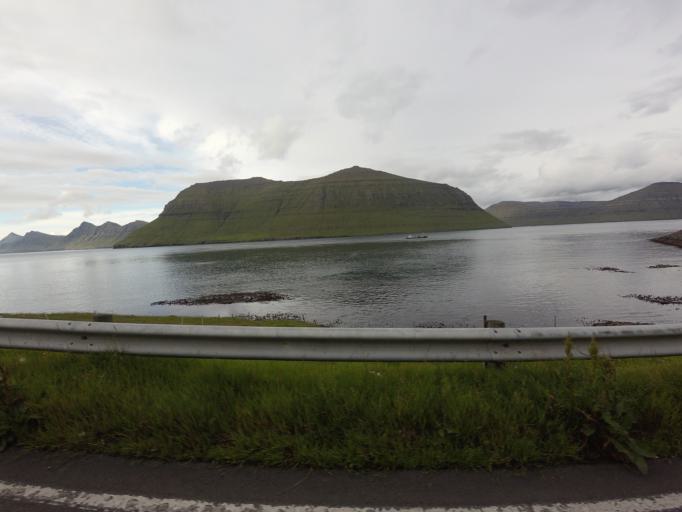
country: FO
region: Eysturoy
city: Eystur
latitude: 62.2137
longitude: -6.7149
